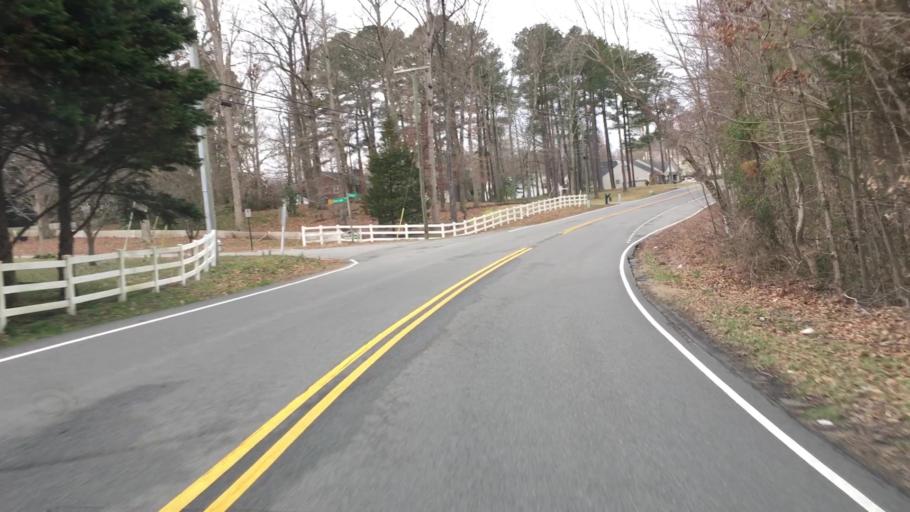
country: US
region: Virginia
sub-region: Henrico County
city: Glen Allen
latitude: 37.6736
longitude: -77.5496
